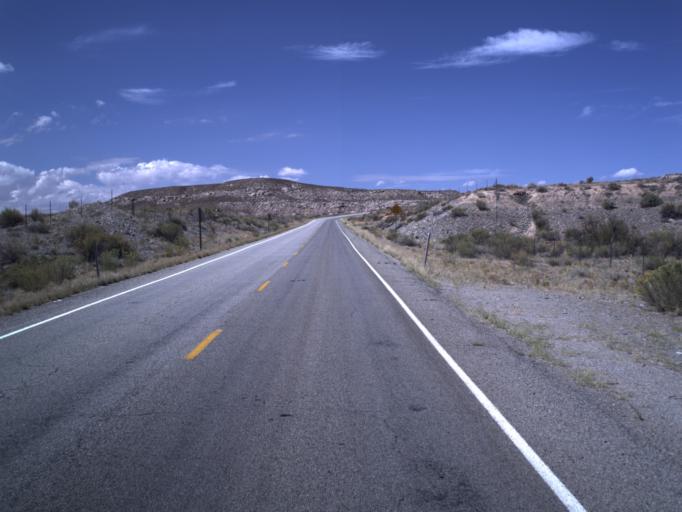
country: US
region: Utah
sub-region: San Juan County
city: Blanding
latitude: 37.2732
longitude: -109.3403
